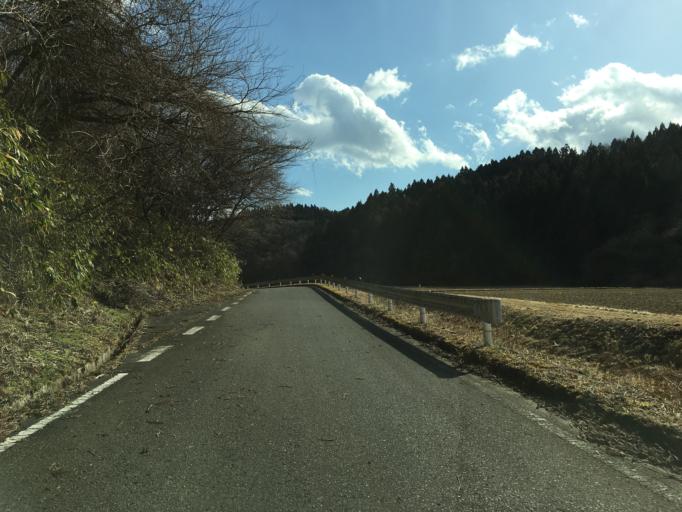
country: JP
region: Fukushima
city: Ishikawa
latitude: 37.2287
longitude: 140.5943
